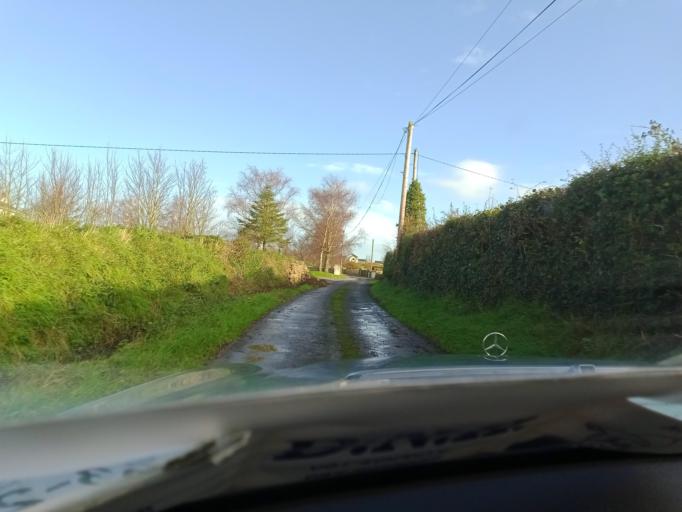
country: IE
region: Leinster
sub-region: Kilkenny
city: Mooncoin
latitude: 52.2773
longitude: -7.2574
